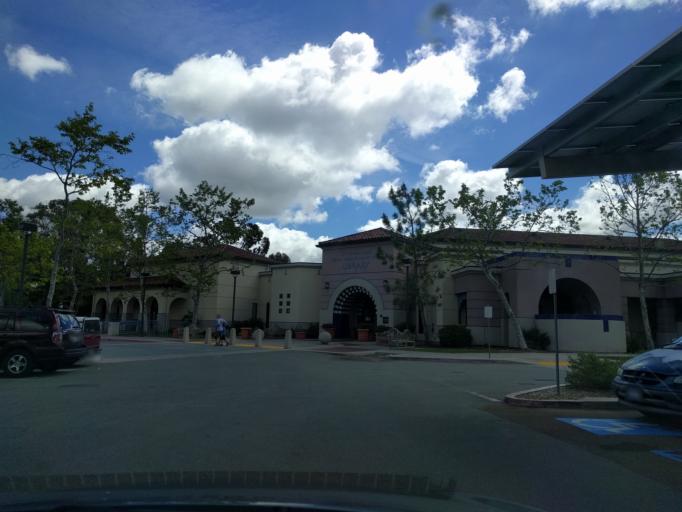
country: US
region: California
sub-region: San Diego County
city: San Diego
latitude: 32.8094
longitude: -117.1342
